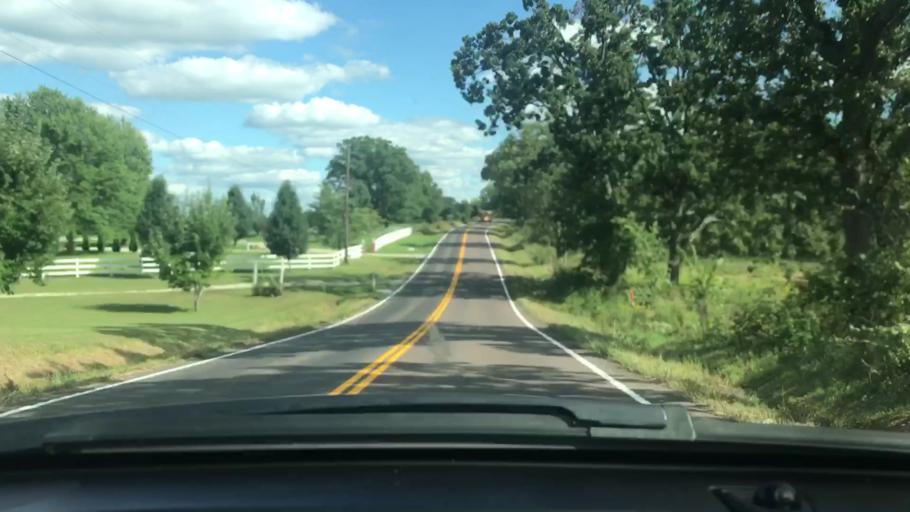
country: US
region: Missouri
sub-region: Wright County
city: Mountain Grove
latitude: 37.2319
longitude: -92.2966
